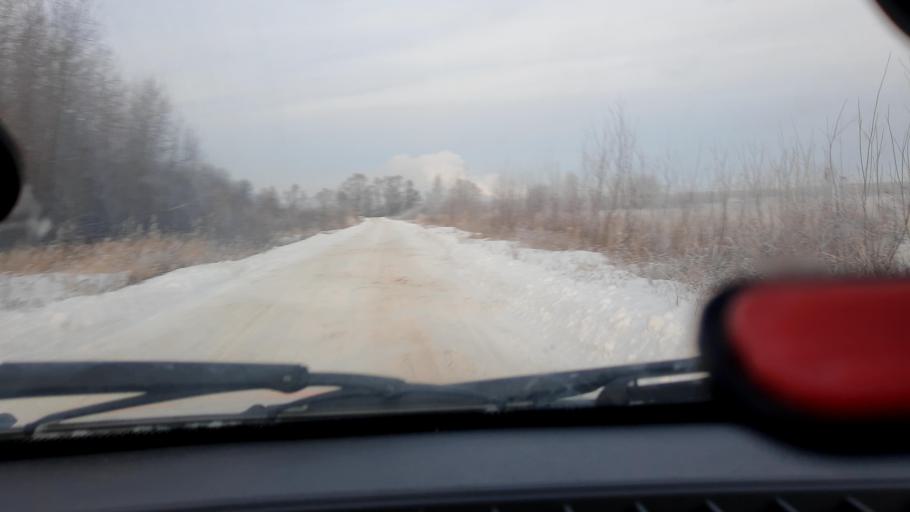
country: RU
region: Bashkortostan
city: Iglino
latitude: 54.7379
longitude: 56.2427
